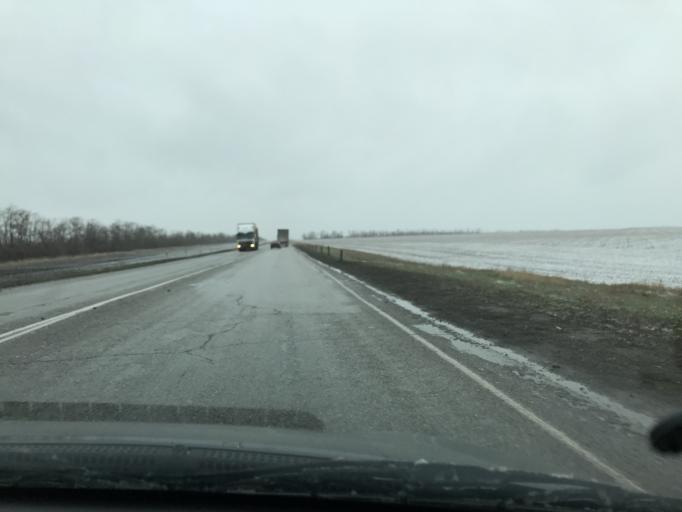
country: RU
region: Rostov
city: Kagal'nitskaya
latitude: 46.8690
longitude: 40.1705
